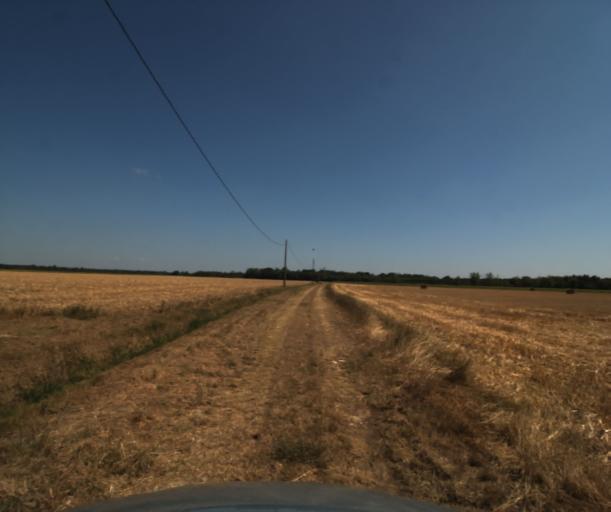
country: FR
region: Midi-Pyrenees
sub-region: Departement de la Haute-Garonne
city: Labastidette
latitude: 43.4726
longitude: 1.2404
